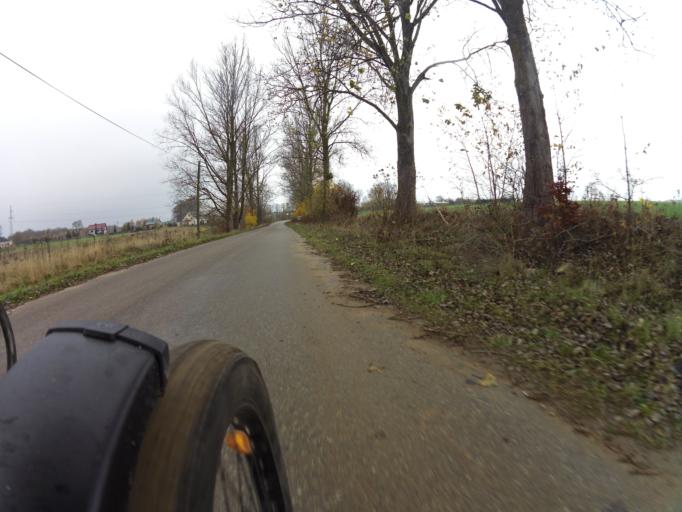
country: PL
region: Pomeranian Voivodeship
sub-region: Powiat pucki
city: Krokowa
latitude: 54.7210
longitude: 18.1380
